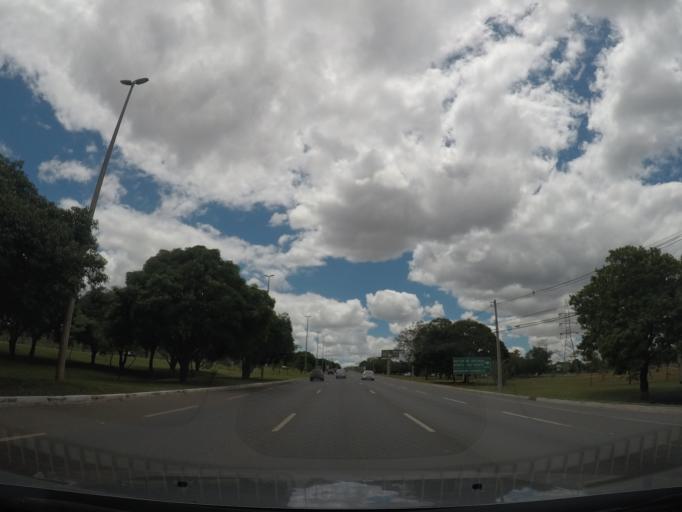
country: BR
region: Federal District
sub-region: Brasilia
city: Brasilia
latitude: -15.7439
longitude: -47.9195
